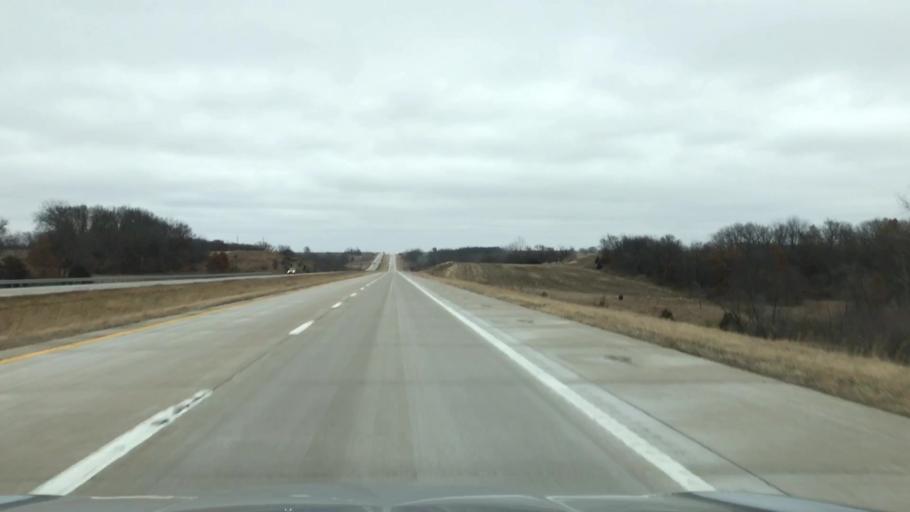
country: US
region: Missouri
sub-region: Livingston County
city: Chillicothe
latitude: 39.7361
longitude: -93.7391
